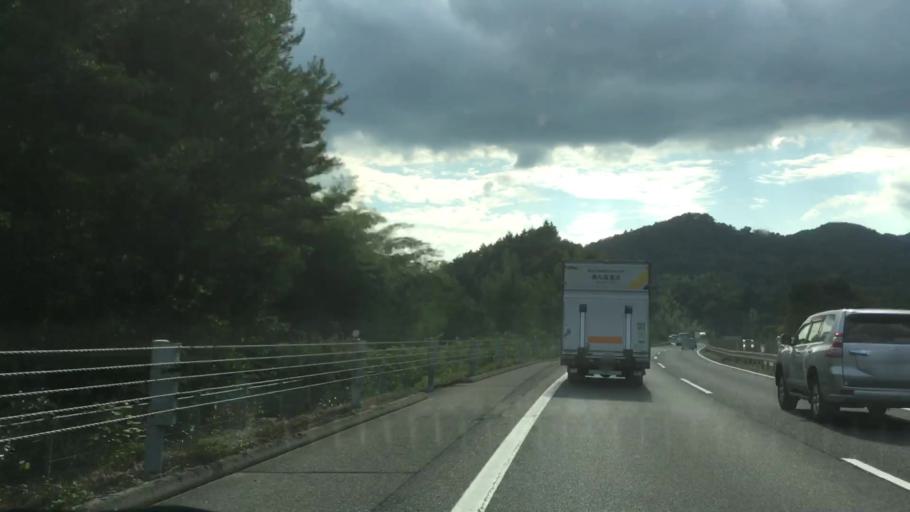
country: JP
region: Yamaguchi
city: Iwakuni
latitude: 34.1423
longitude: 132.1227
